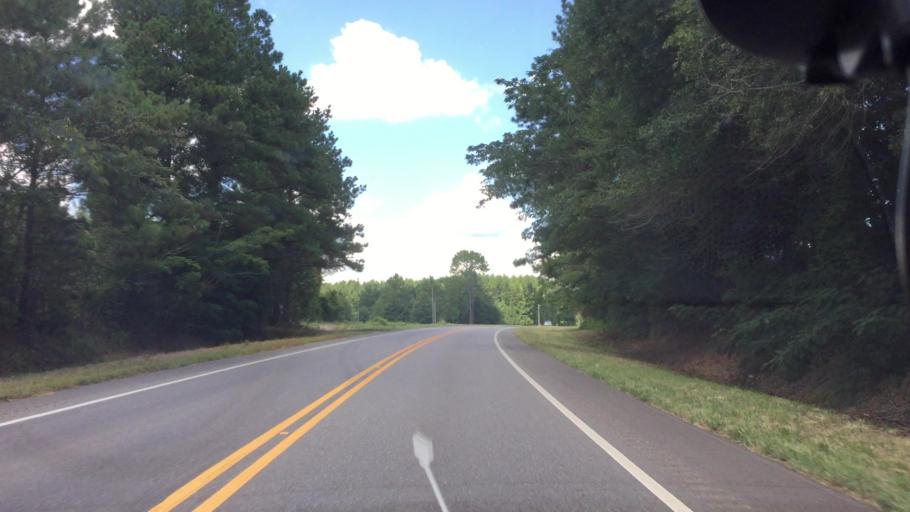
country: US
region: Alabama
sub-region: Pike County
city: Brundidge
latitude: 31.5976
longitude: -85.9465
